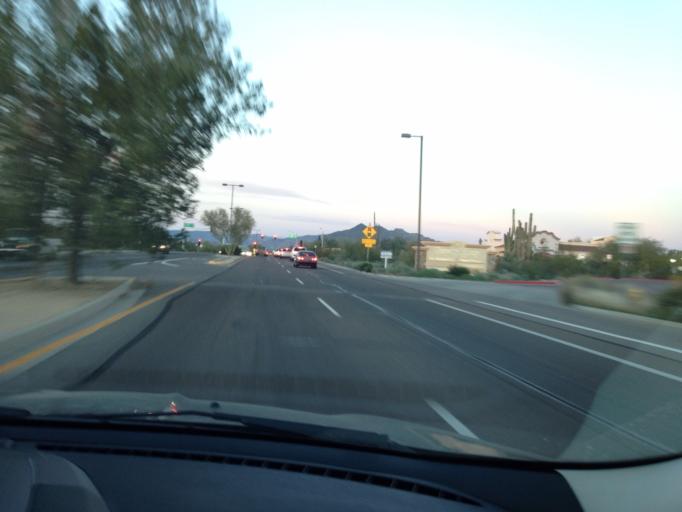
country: US
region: Arizona
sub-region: Maricopa County
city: Cave Creek
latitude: 33.7652
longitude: -111.9848
